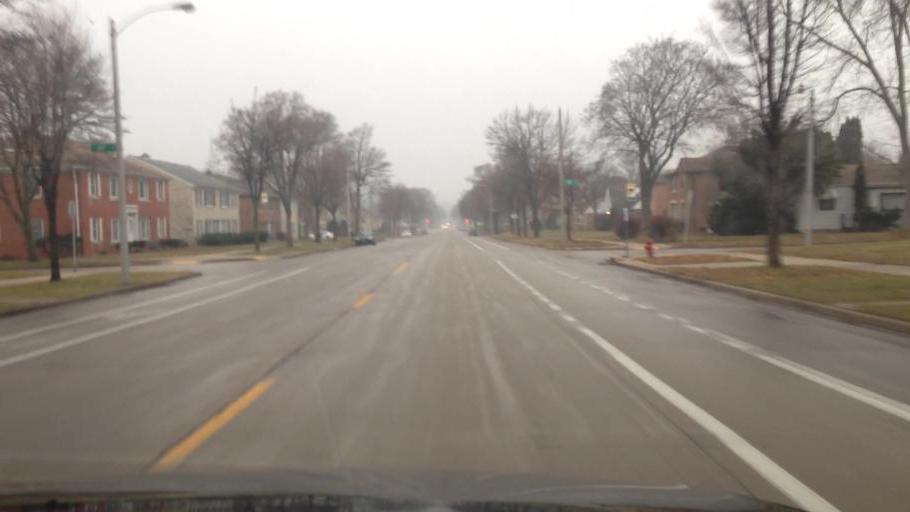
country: US
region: Wisconsin
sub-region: Milwaukee County
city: Wauwatosa
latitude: 43.0678
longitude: -88.0219
